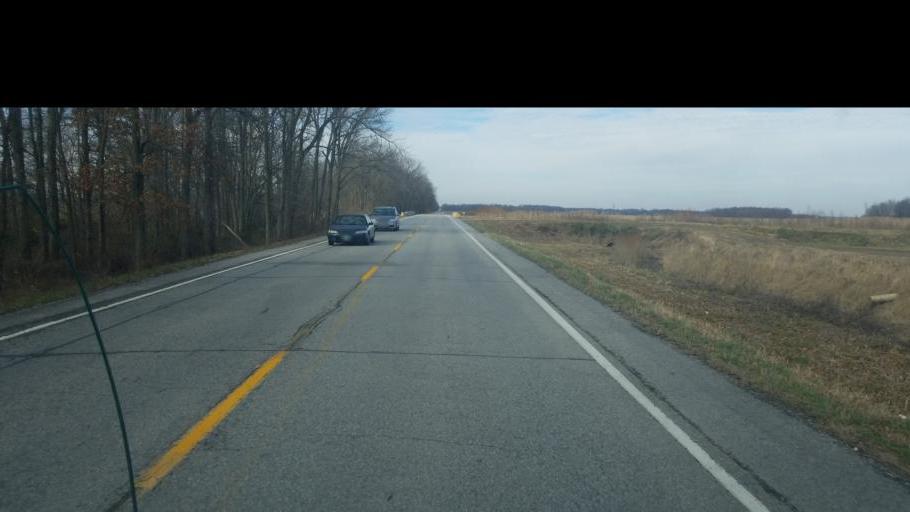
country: US
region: Illinois
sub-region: White County
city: Norris City
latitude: 37.9570
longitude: -88.4721
